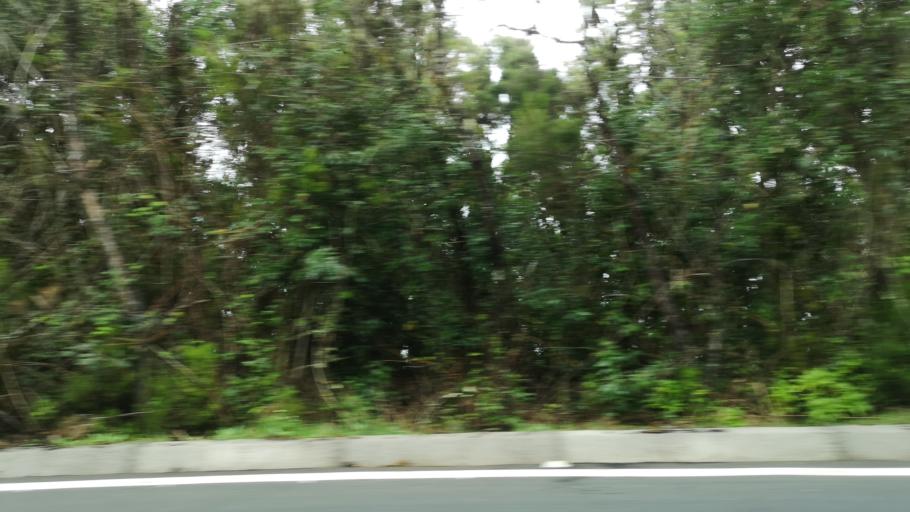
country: ES
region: Canary Islands
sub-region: Provincia de Santa Cruz de Tenerife
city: Vallehermosa
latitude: 28.1442
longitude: -17.2861
